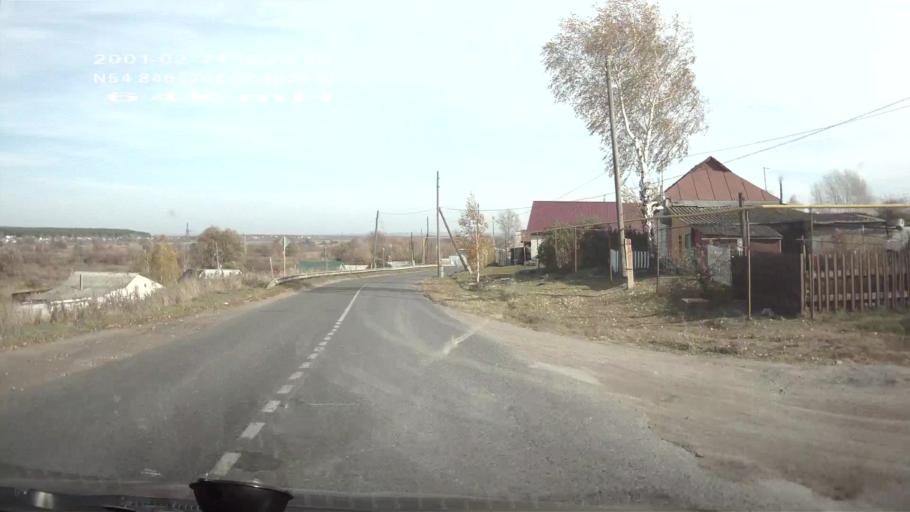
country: RU
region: Chuvashia
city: Alatyr'
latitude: 54.8466
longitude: 46.4929
